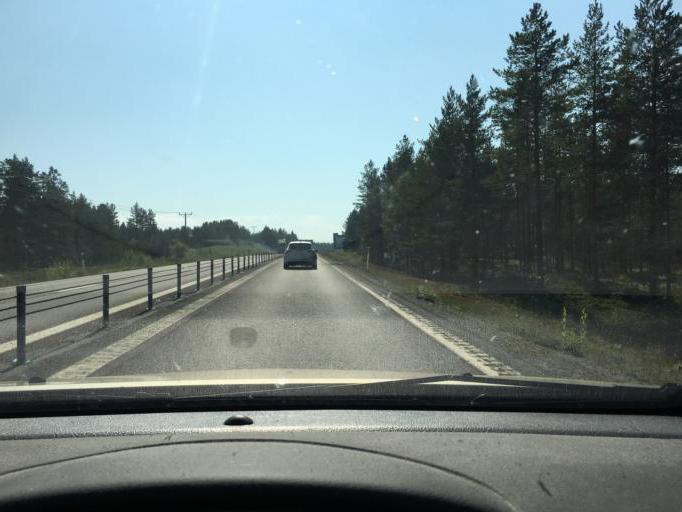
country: SE
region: Norrbotten
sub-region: Lulea Kommun
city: Gammelstad
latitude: 65.6040
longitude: 22.0507
